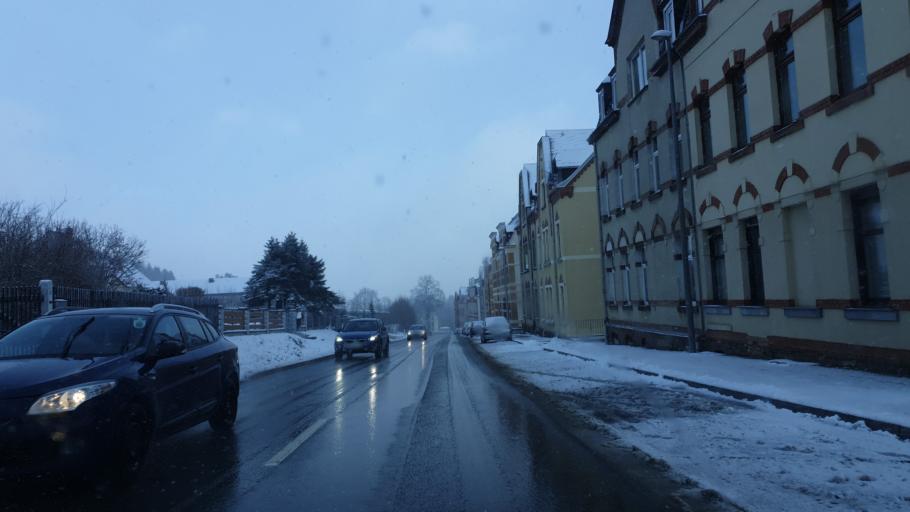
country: DE
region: Saxony
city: Oelsnitz
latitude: 50.4042
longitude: 12.1557
